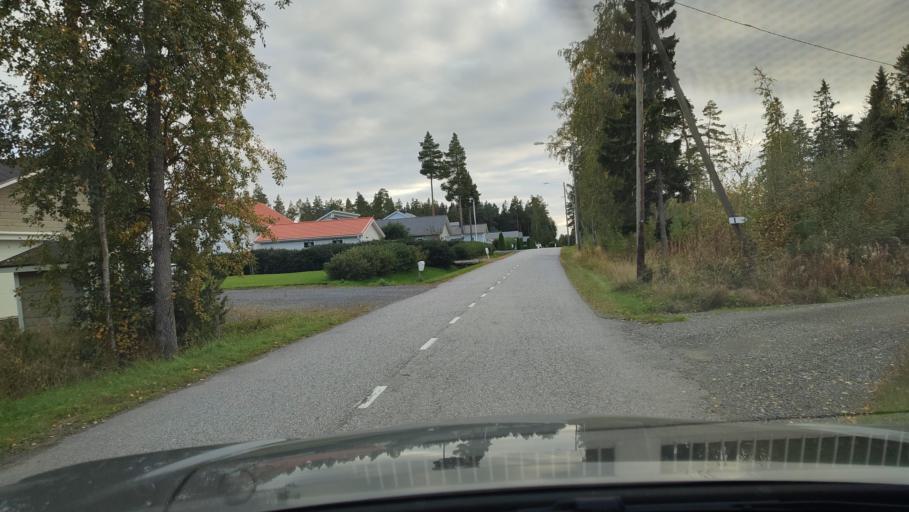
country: FI
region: Ostrobothnia
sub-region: Sydosterbotten
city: Kristinestad
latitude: 62.2566
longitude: 21.3841
